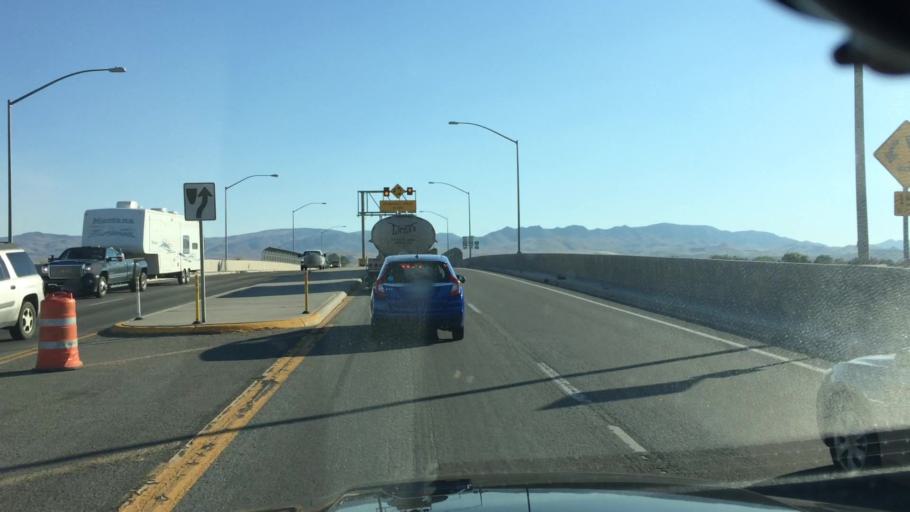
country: US
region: Nevada
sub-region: Lyon County
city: Fernley
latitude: 39.6058
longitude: -119.2249
